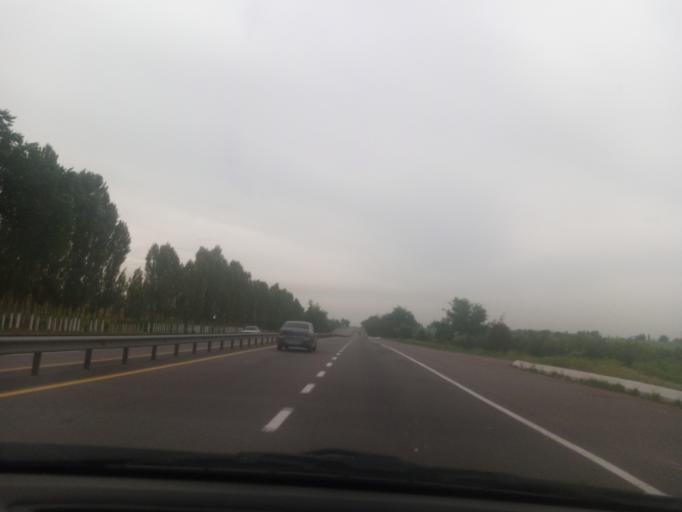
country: UZ
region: Toshkent
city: Tuytepa
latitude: 41.0908
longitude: 69.4627
